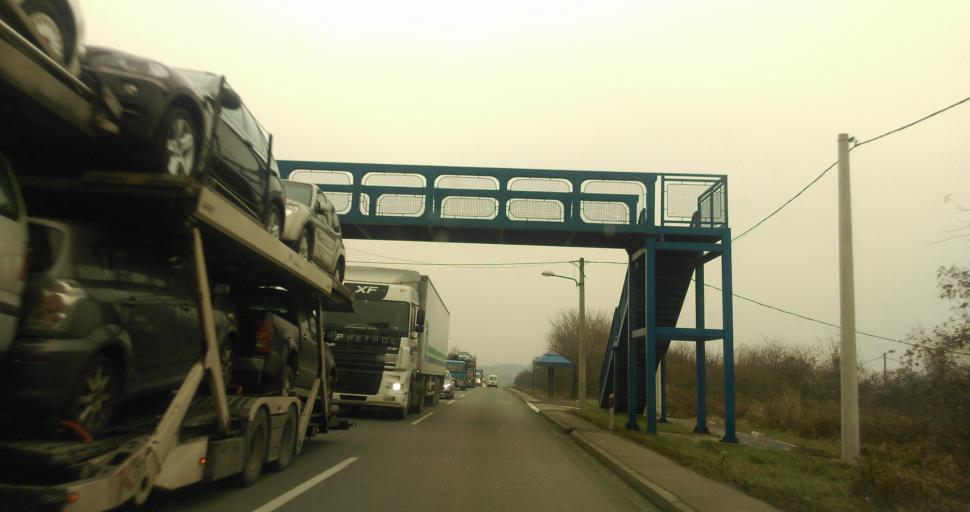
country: RS
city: Rusanj
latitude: 44.7160
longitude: 20.4938
